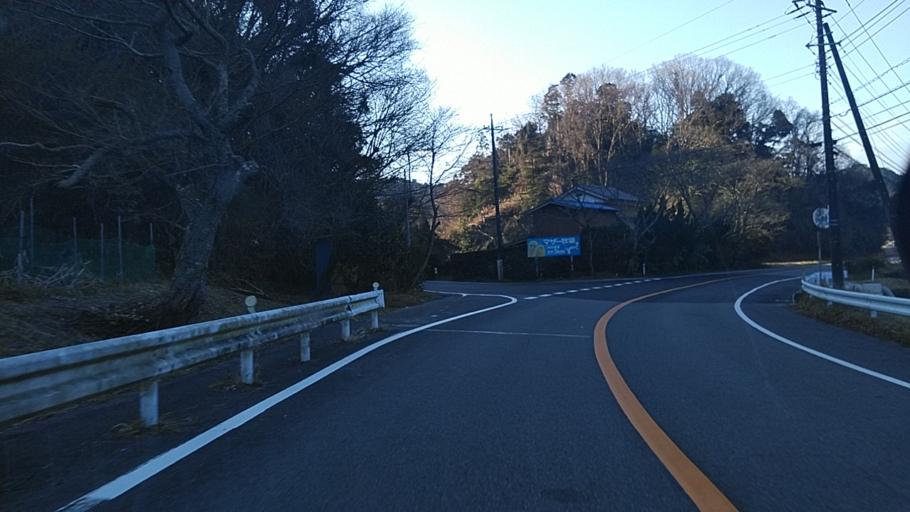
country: JP
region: Chiba
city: Kimitsu
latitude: 35.2751
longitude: 139.9230
